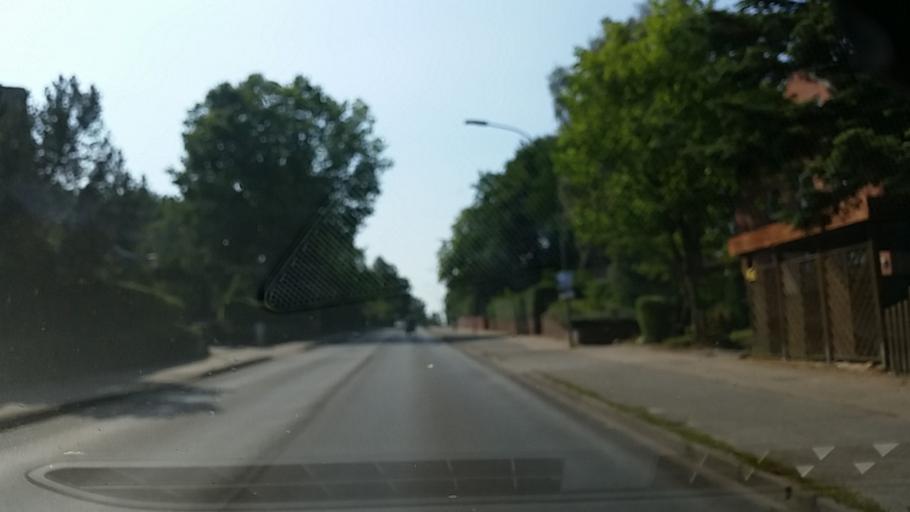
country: DE
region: Schleswig-Holstein
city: Glinde
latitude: 53.5399
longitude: 10.2066
